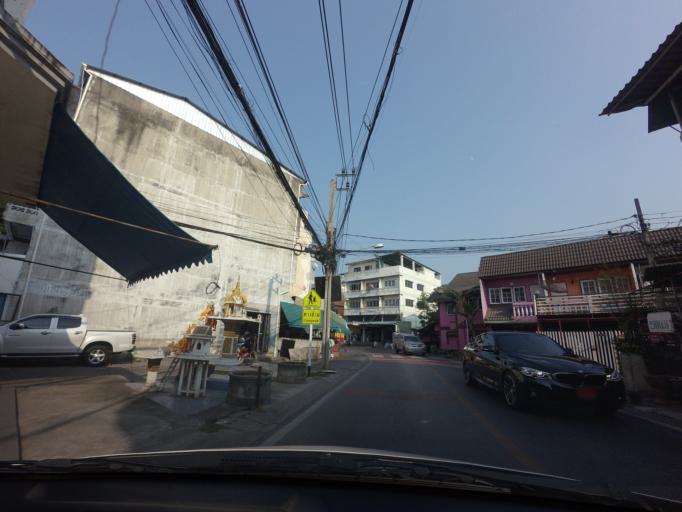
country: TH
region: Bangkok
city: Taling Chan
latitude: 13.8038
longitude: 100.4094
